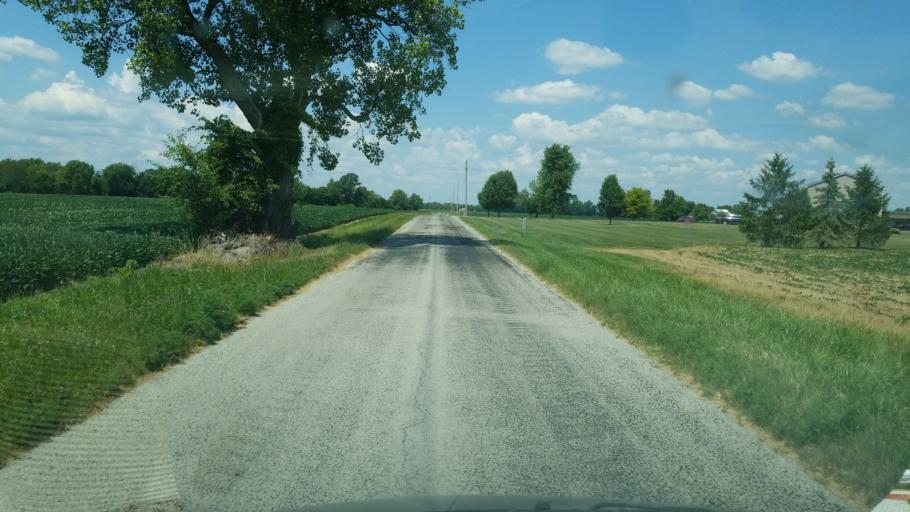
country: US
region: Ohio
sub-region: Madison County
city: Plain City
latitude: 40.0688
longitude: -83.3996
